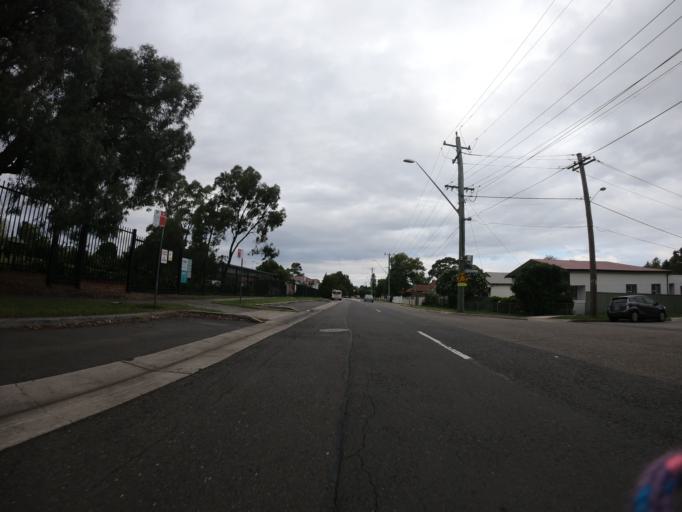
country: AU
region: New South Wales
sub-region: Parramatta
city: Granville
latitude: -33.8376
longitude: 151.0051
